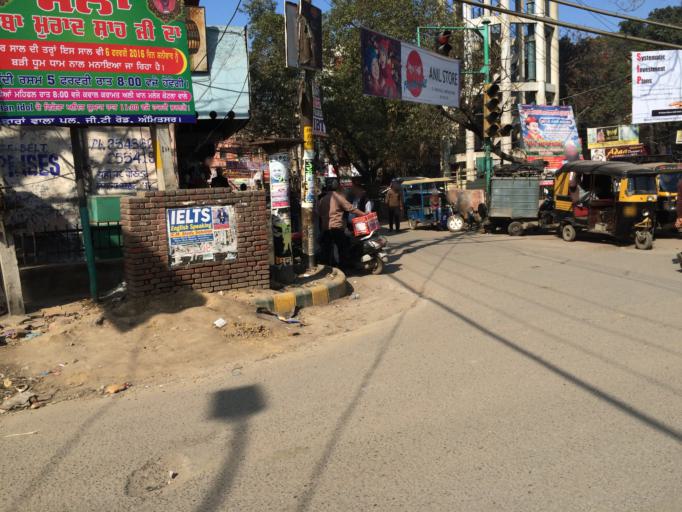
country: IN
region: Punjab
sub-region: Amritsar
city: Amritsar
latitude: 31.6307
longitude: 74.8729
